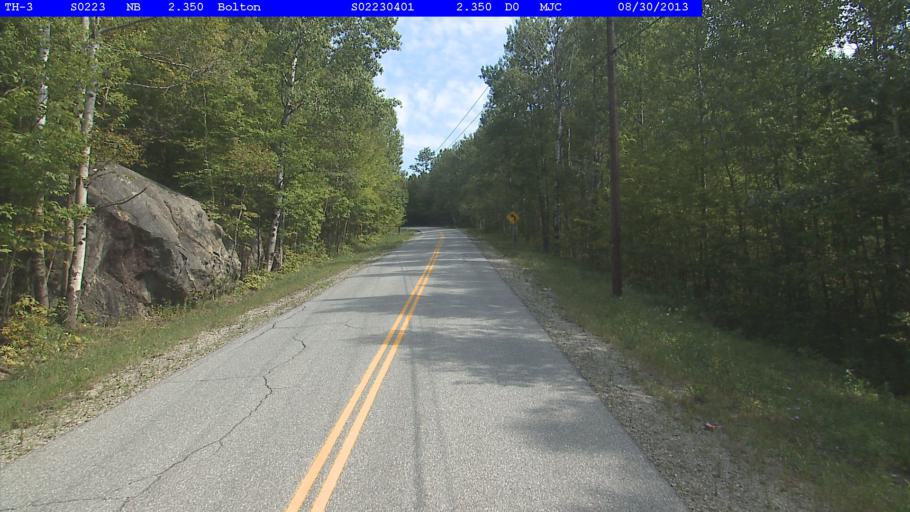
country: US
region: Vermont
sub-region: Washington County
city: Waterbury
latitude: 44.4024
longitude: -72.8757
